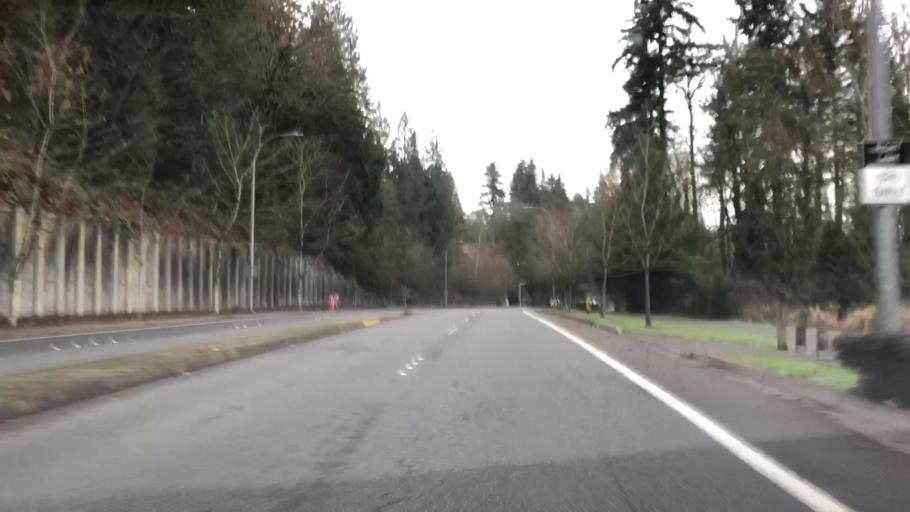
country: US
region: Washington
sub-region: King County
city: Redmond
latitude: 47.6603
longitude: -122.1244
